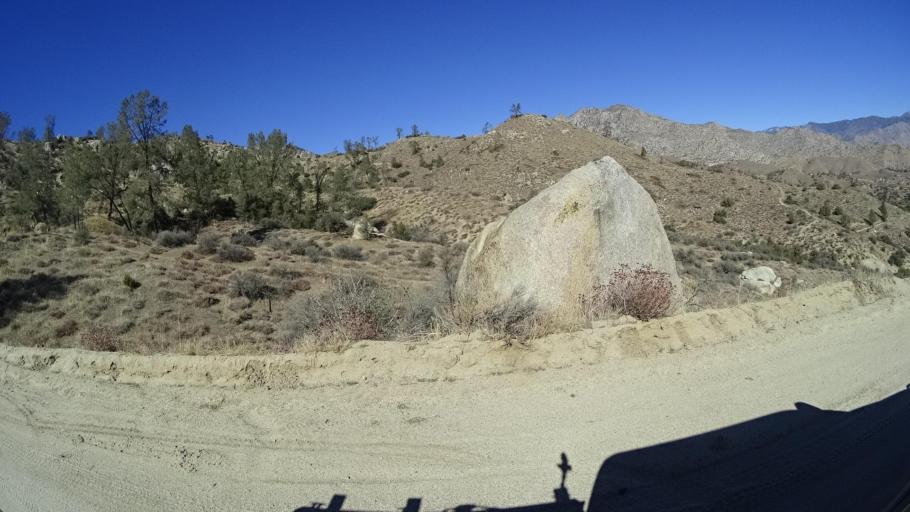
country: US
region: California
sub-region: Kern County
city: Wofford Heights
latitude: 35.6998
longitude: -118.4855
